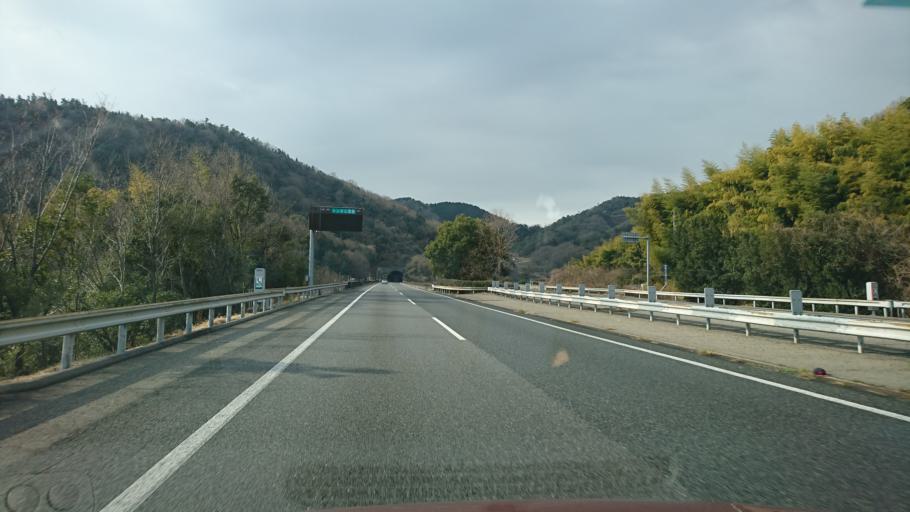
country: JP
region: Okayama
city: Kamogatacho-kamogata
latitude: 34.5616
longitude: 133.6221
